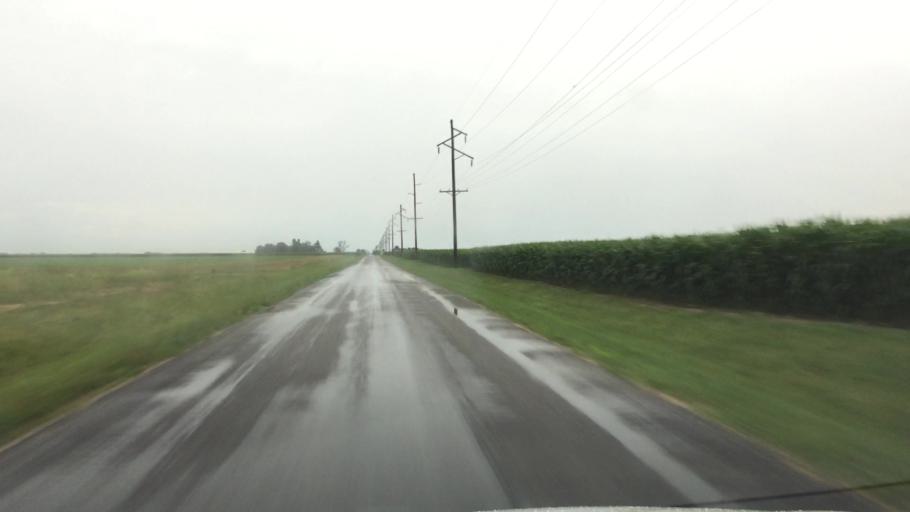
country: US
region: Illinois
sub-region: Hancock County
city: Nauvoo
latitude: 40.5168
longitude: -91.2693
